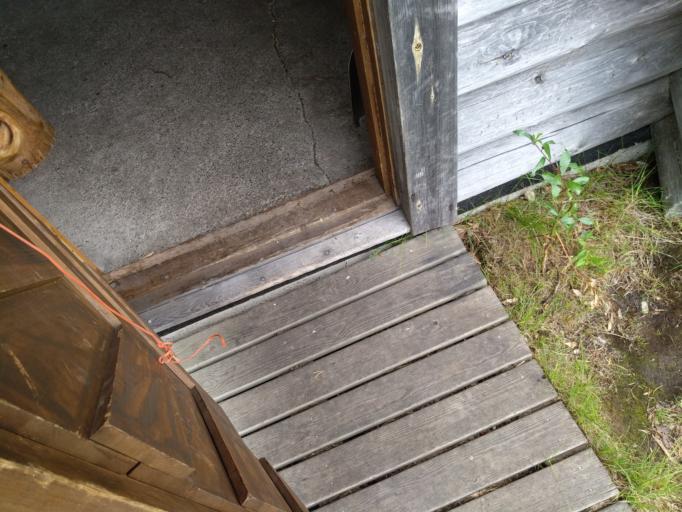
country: FI
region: Kainuu
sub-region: Kajaani
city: Ristijaervi
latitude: 64.6737
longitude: 28.1198
